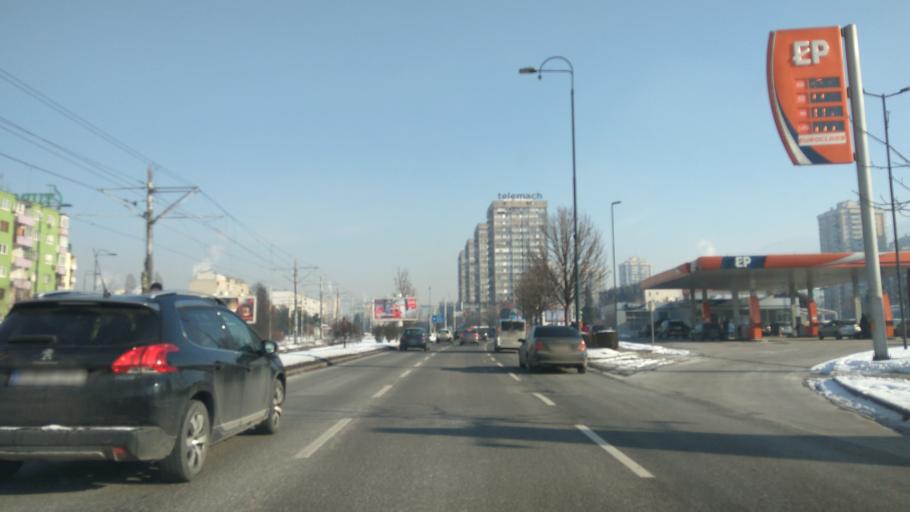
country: BA
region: Federation of Bosnia and Herzegovina
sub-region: Kanton Sarajevo
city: Sarajevo
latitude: 43.8497
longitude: 18.3704
